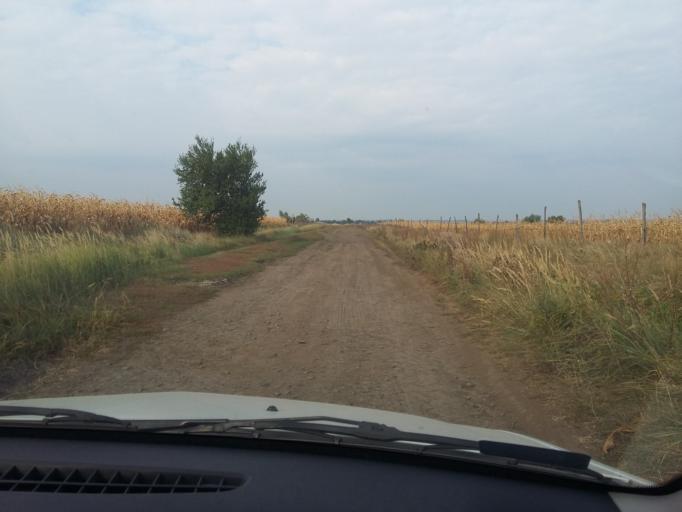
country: HU
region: Borsod-Abauj-Zemplen
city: Taktaharkany
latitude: 48.1353
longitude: 21.1084
